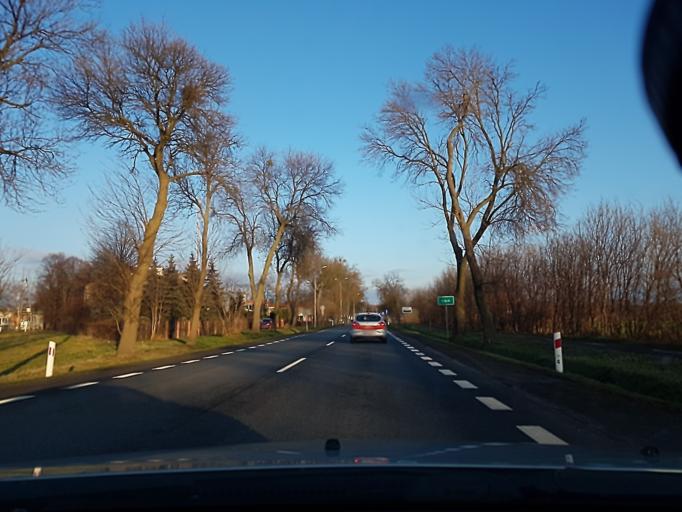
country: PL
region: Masovian Voivodeship
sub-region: Powiat plocki
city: Lack
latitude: 52.4644
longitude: 19.6061
